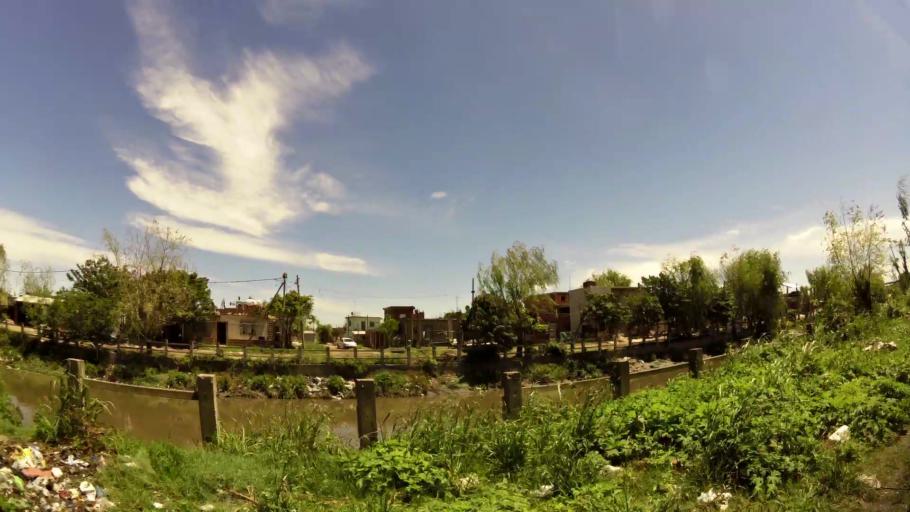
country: AR
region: Buenos Aires
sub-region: Partido de Quilmes
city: Quilmes
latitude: -34.7403
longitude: -58.3083
